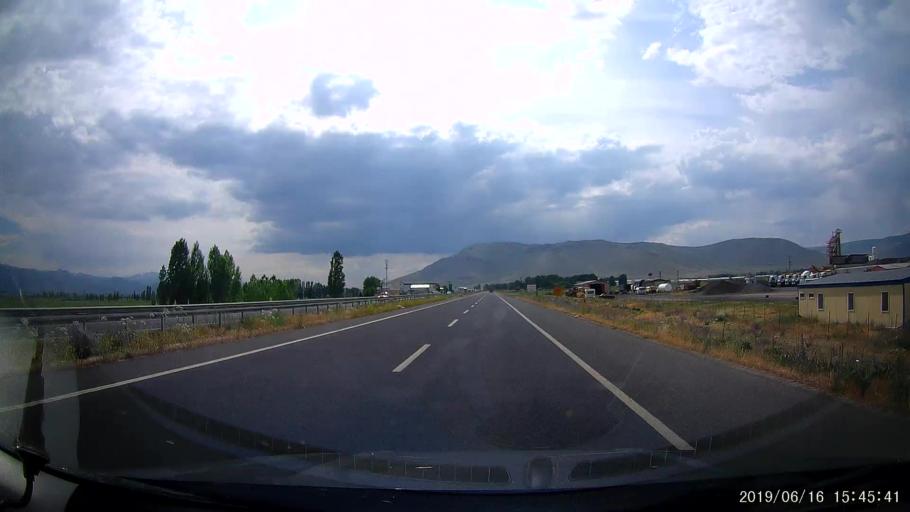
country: TR
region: Erzurum
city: Pasinler
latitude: 39.9894
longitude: 41.7652
